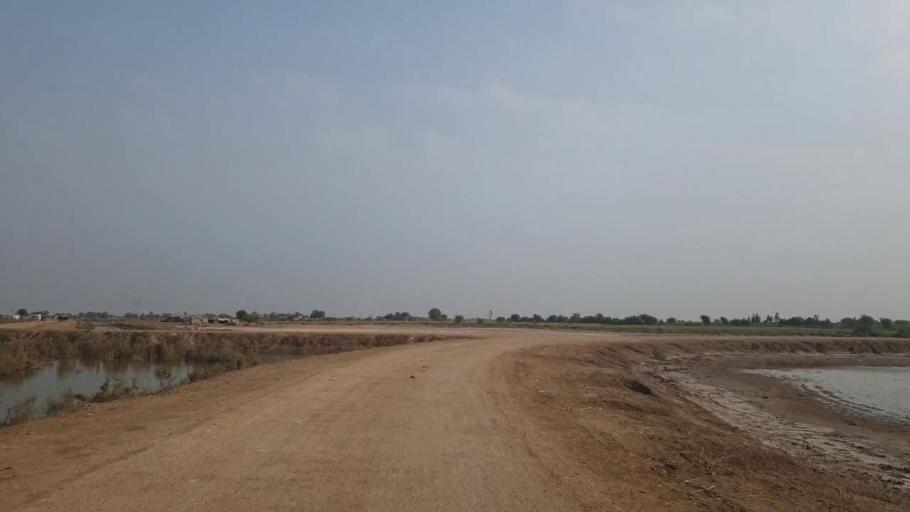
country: PK
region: Sindh
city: Badin
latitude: 24.6000
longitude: 68.7009
